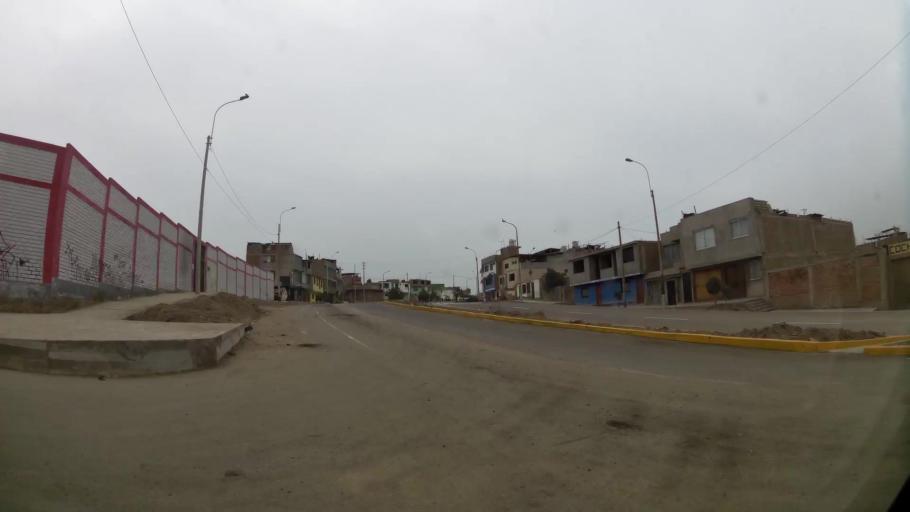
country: PE
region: Lima
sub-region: Lima
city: Surco
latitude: -12.2004
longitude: -76.9766
